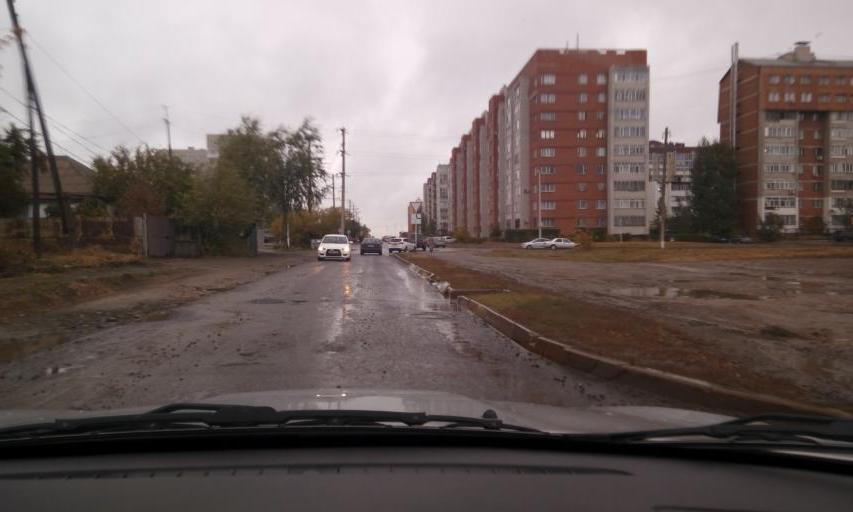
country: KZ
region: Astana Qalasy
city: Astana
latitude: 51.1643
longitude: 71.4002
